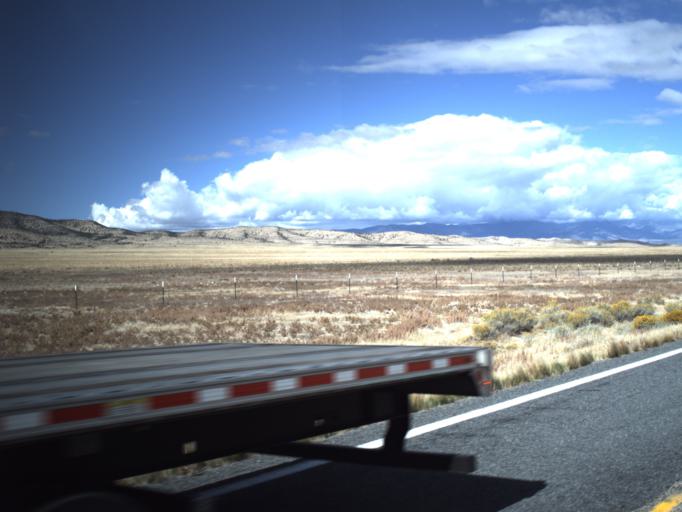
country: US
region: Utah
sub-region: Beaver County
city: Milford
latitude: 38.6596
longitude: -113.8761
